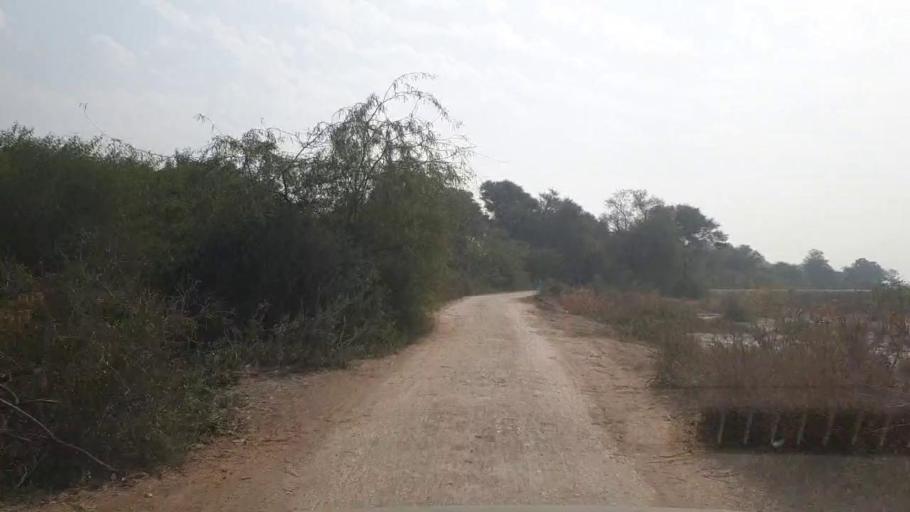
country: PK
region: Sindh
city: Hala
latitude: 25.7803
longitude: 68.4362
